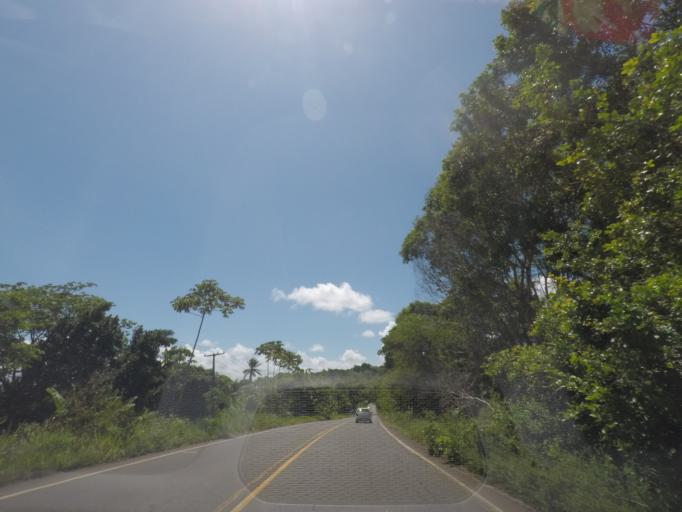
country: BR
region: Bahia
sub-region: Valenca
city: Valenca
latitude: -13.3287
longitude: -39.0494
